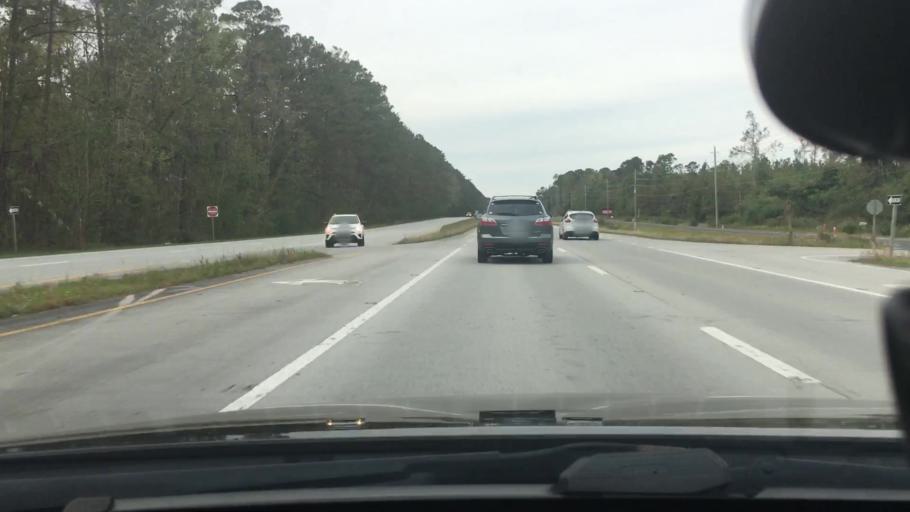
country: US
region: North Carolina
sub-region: Craven County
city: Neuse Forest
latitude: 34.9767
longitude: -76.9753
